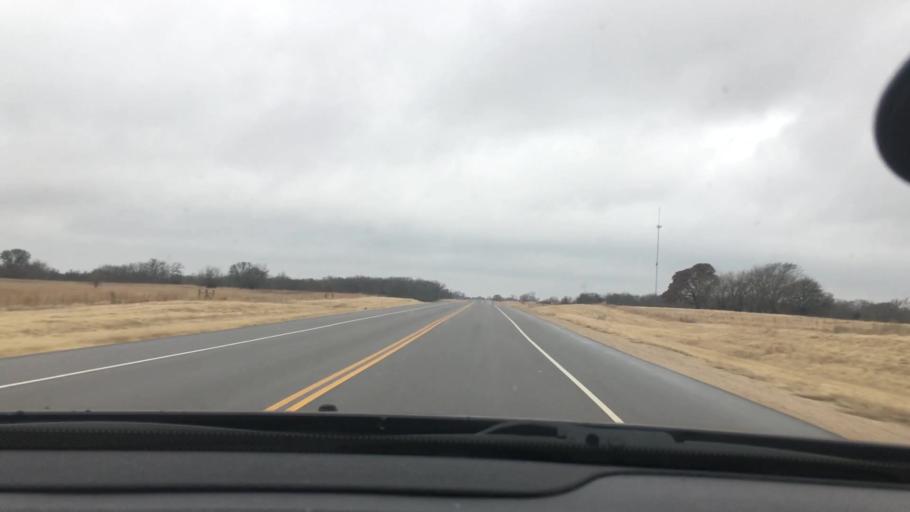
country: US
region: Oklahoma
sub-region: Johnston County
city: Tishomingo
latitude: 34.3256
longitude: -96.6624
